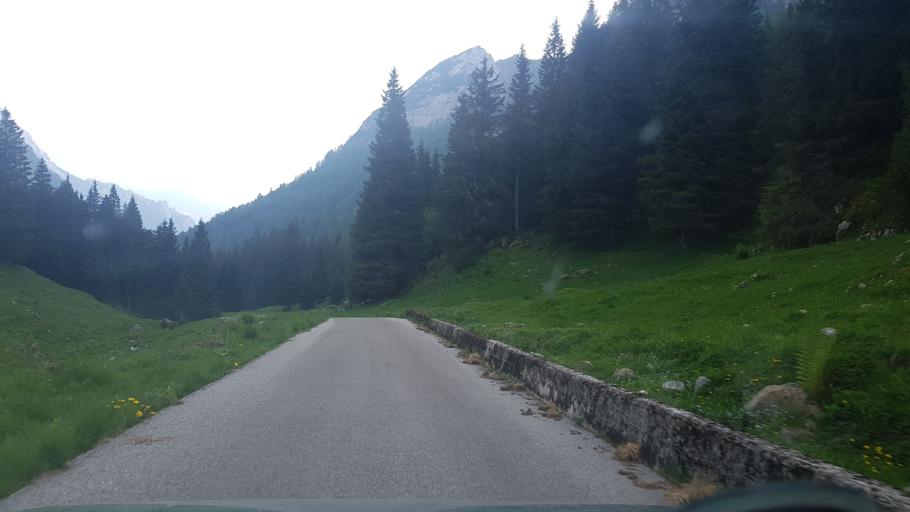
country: IT
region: Friuli Venezia Giulia
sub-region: Provincia di Udine
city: Paularo
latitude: 46.5651
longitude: 13.1721
